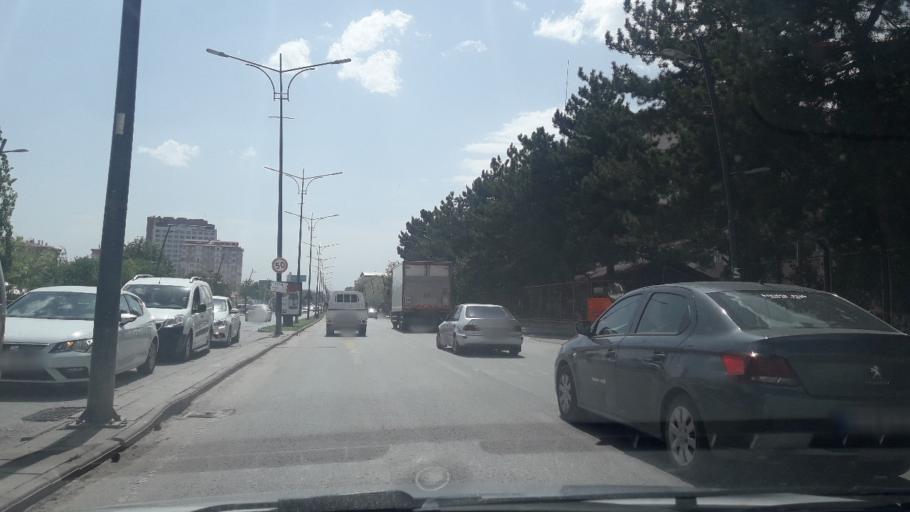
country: TR
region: Sivas
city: Sivas
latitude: 39.7392
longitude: 37.0019
